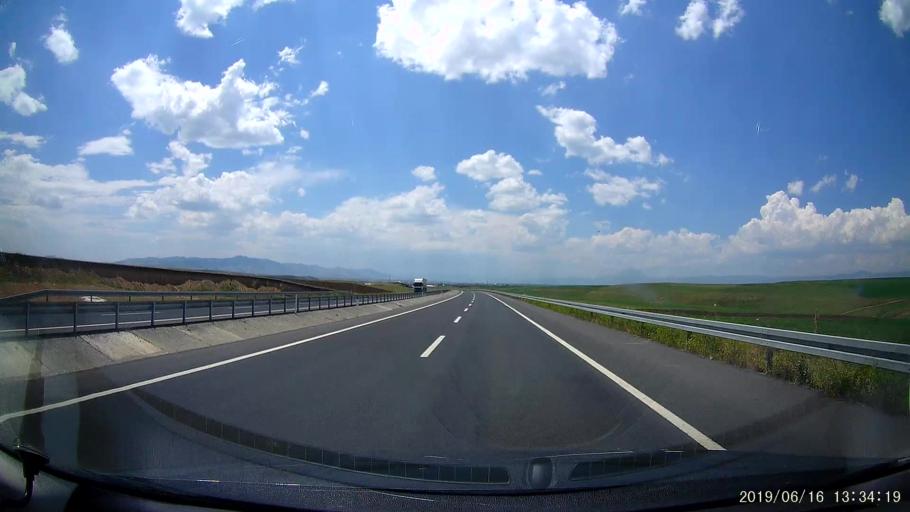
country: TR
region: Agri
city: Agri
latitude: 39.7124
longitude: 43.1299
